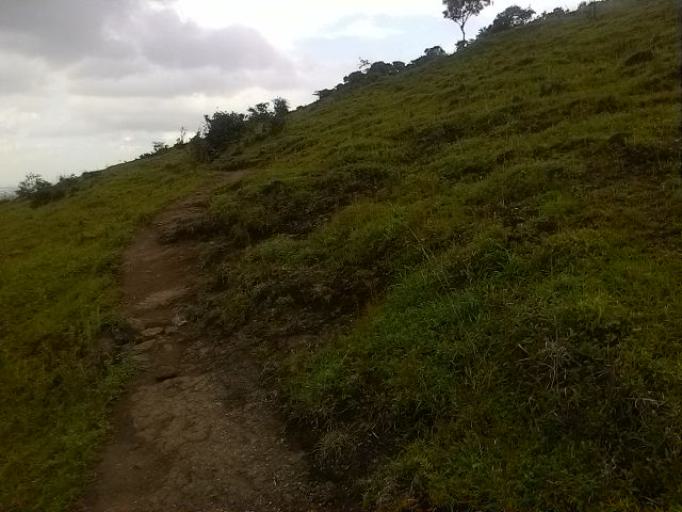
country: IN
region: Maharashtra
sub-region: Pune Division
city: Khadki
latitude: 18.5494
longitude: 73.7850
